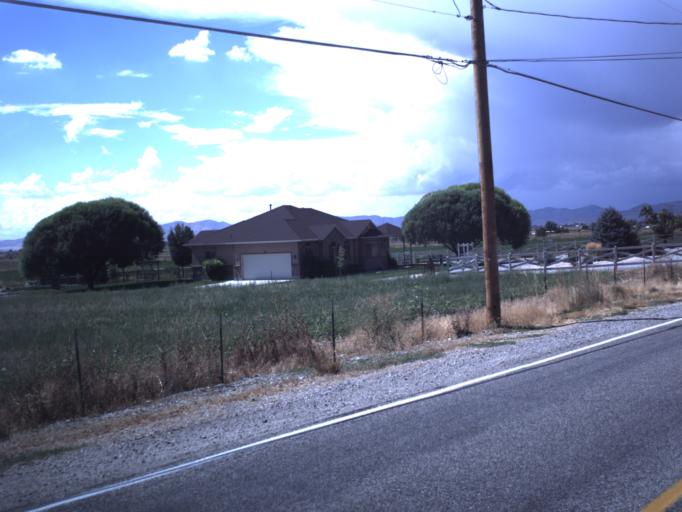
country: US
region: Utah
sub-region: Box Elder County
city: Honeyville
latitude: 41.6250
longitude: -112.0739
